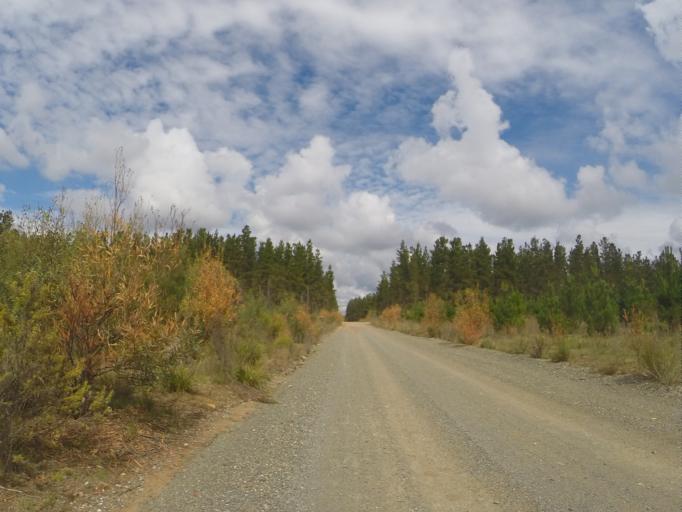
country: AU
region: New South Wales
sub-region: Wingecarribee
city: Moss Vale
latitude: -34.5262
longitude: 150.2282
